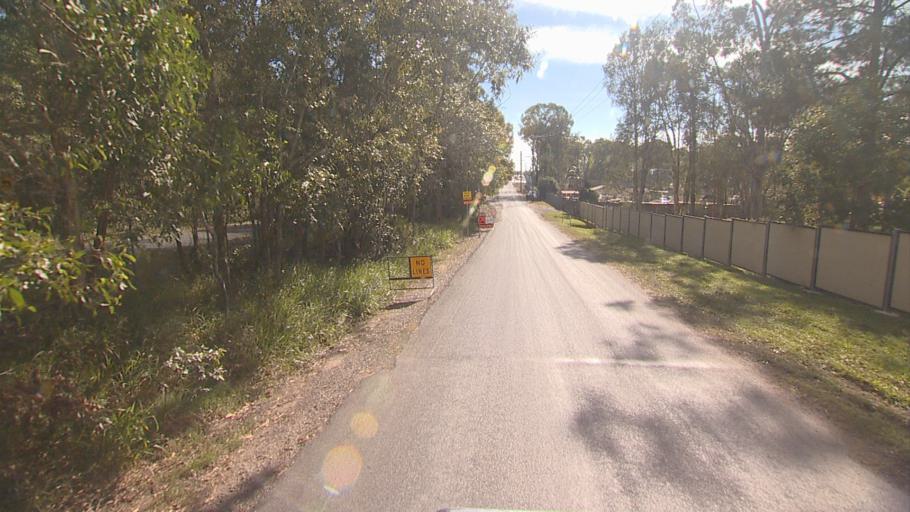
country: AU
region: Queensland
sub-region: Brisbane
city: Forest Lake
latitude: -27.6507
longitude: 152.9837
